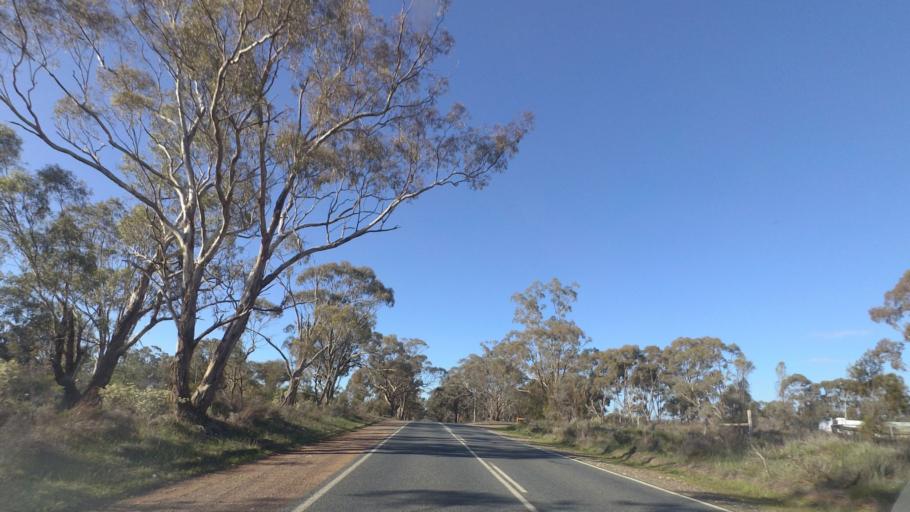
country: AU
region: Victoria
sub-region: Greater Bendigo
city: Epsom
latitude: -36.6769
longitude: 144.3884
